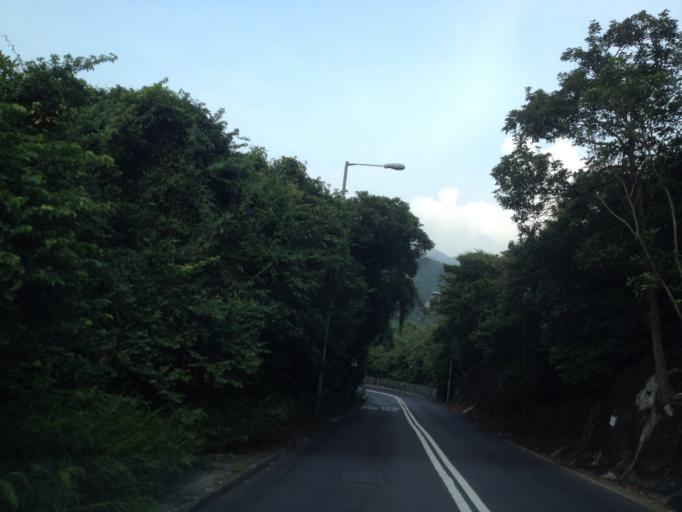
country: HK
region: Wanchai
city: Wan Chai
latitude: 22.2477
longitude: 114.2222
